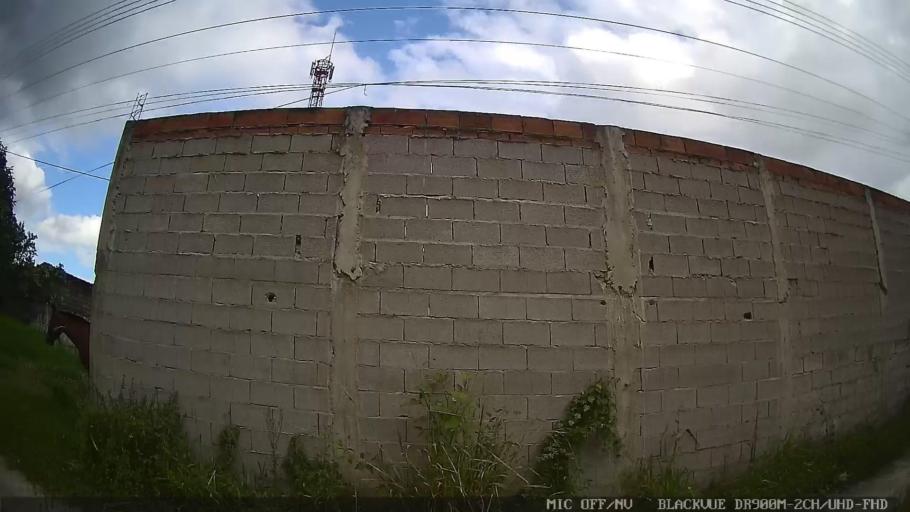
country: BR
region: Sao Paulo
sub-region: Caraguatatuba
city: Caraguatatuba
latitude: -23.6266
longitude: -45.4361
